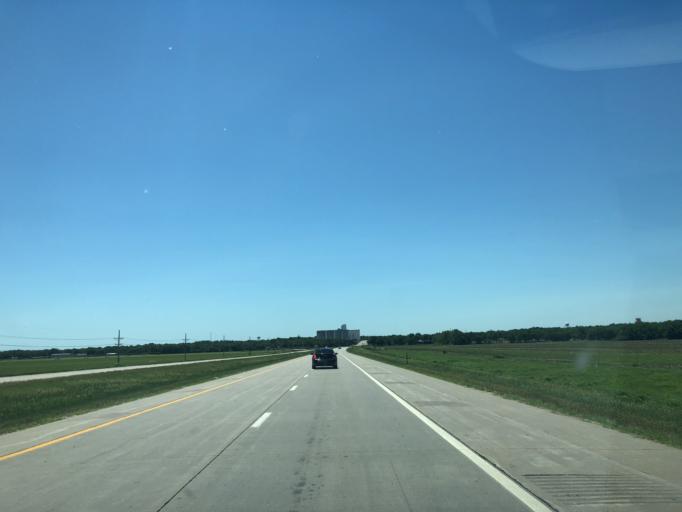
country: US
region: Kansas
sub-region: Cloud County
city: Concordia
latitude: 39.5875
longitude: -97.6585
